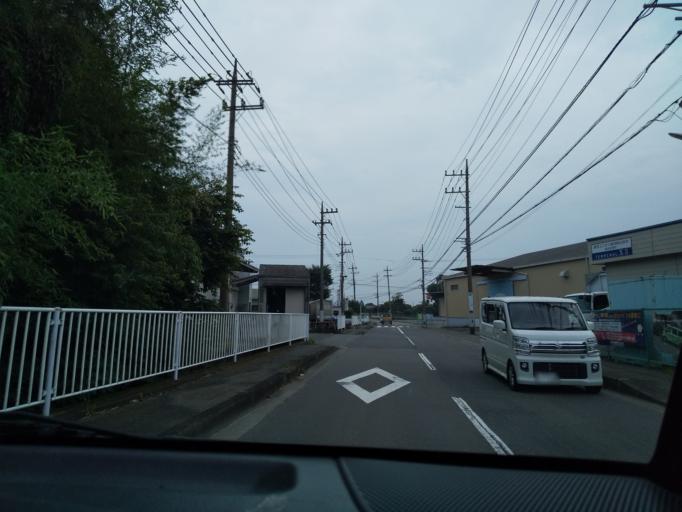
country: JP
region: Kanagawa
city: Atsugi
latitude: 35.4120
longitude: 139.3904
